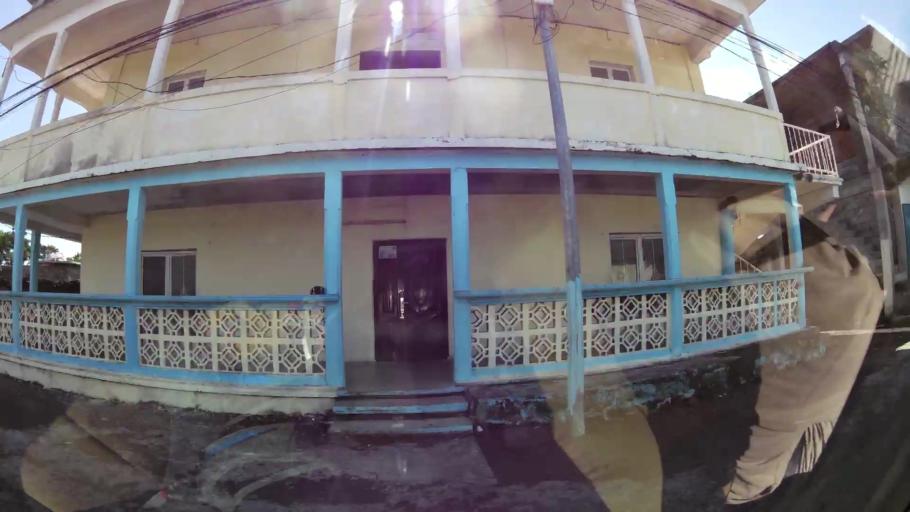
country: KM
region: Grande Comore
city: Mavingouni
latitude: -11.7473
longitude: 43.2367
